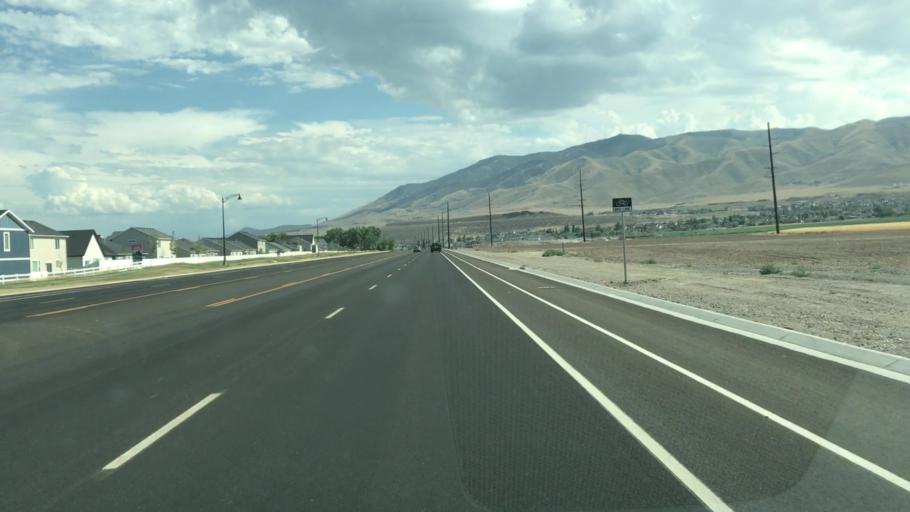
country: US
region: Utah
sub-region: Utah County
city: Saratoga Springs
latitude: 40.3523
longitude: -111.9165
